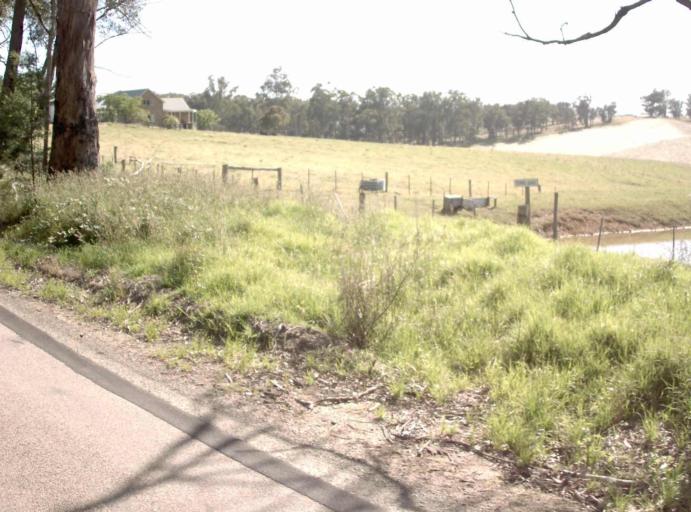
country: AU
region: Victoria
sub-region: East Gippsland
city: Lakes Entrance
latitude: -37.5239
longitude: 148.1611
